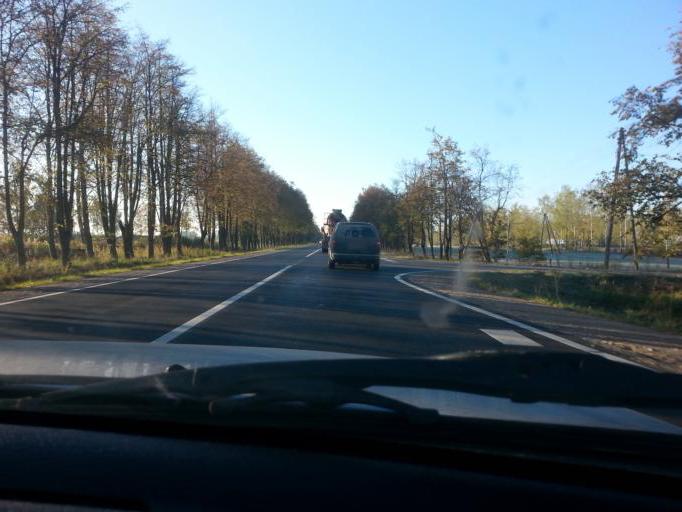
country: LV
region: Jelgava
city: Jelgava
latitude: 56.5053
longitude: 23.7008
